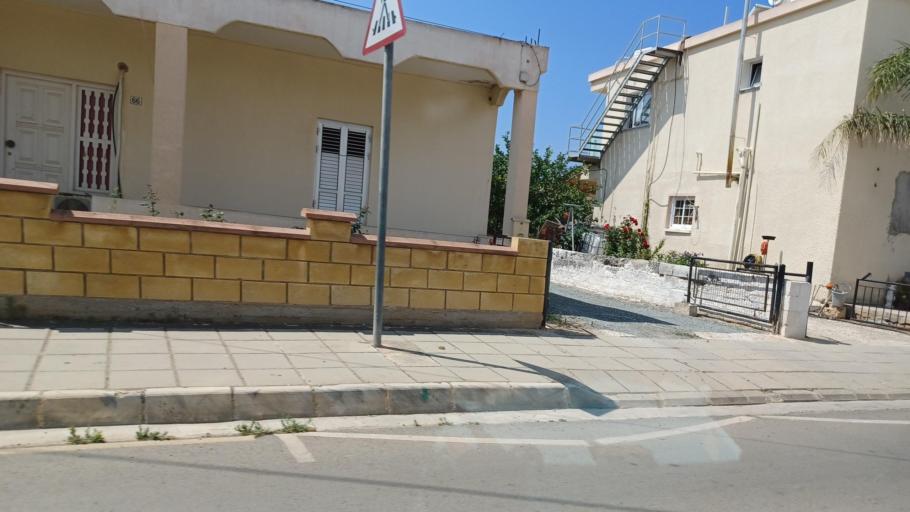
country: CY
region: Ammochostos
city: Liopetri
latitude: 34.9781
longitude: 33.8557
